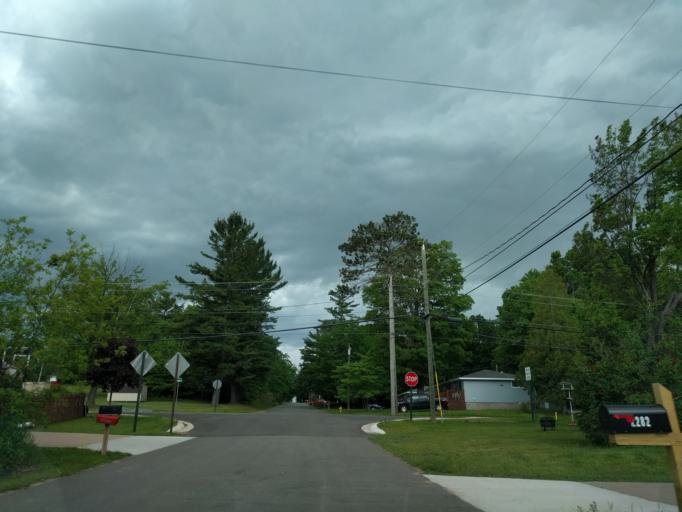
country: US
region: Michigan
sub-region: Marquette County
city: Trowbridge Park
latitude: 46.5542
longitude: -87.4370
